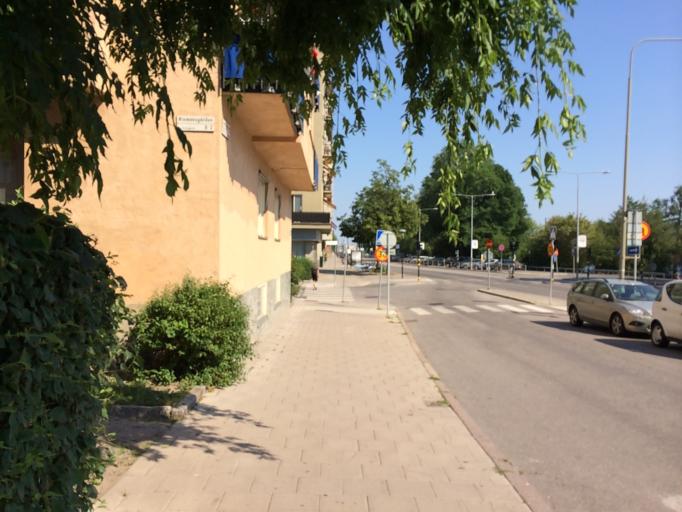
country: SE
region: Stockholm
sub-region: Stockholms Kommun
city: Stockholm
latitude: 59.3285
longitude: 18.0310
